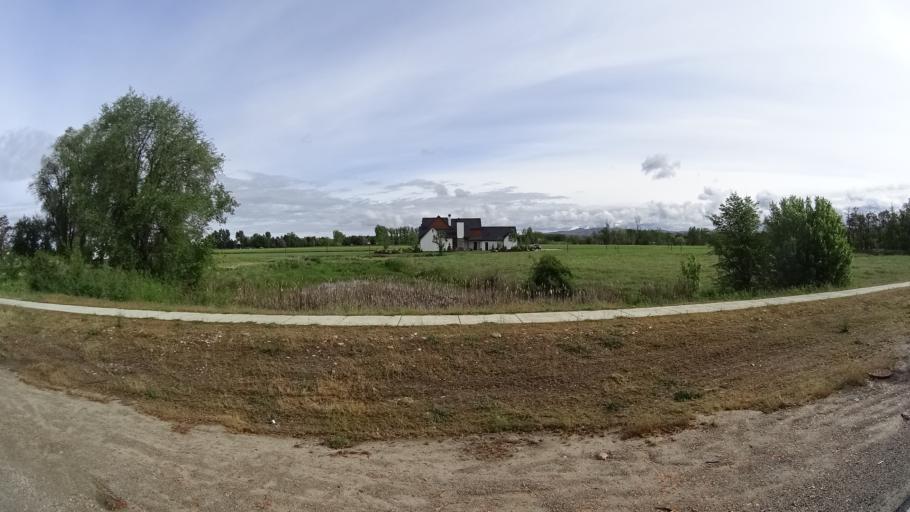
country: US
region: Idaho
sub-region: Ada County
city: Eagle
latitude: 43.7208
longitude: -116.3772
